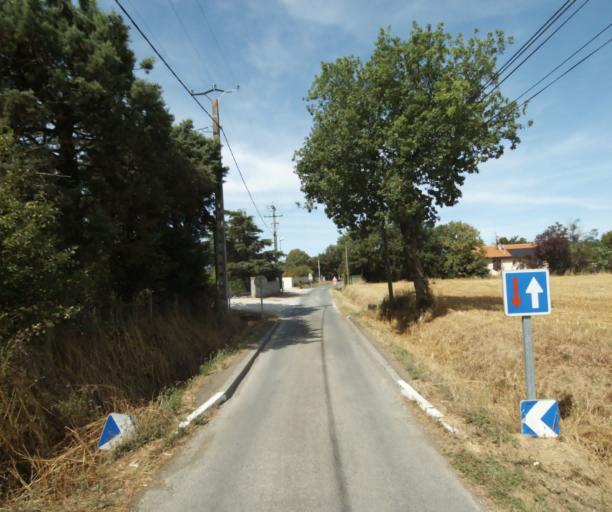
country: FR
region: Midi-Pyrenees
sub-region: Departement de la Haute-Garonne
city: Revel
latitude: 43.5095
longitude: 2.0332
